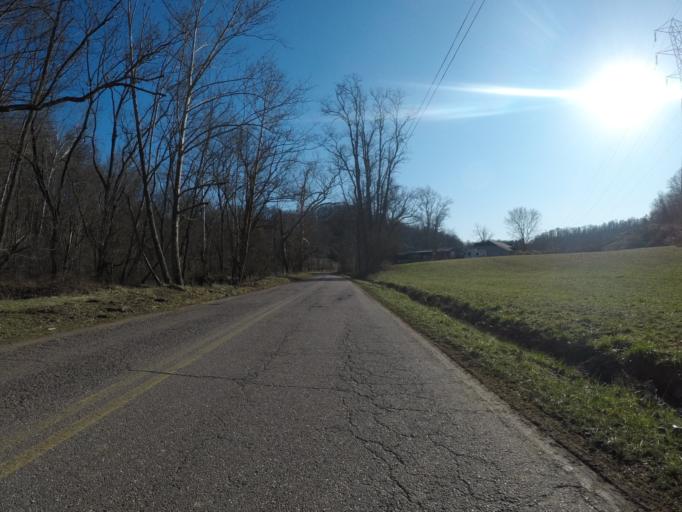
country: US
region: West Virginia
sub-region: Cabell County
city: Huntington
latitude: 38.5076
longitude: -82.4487
